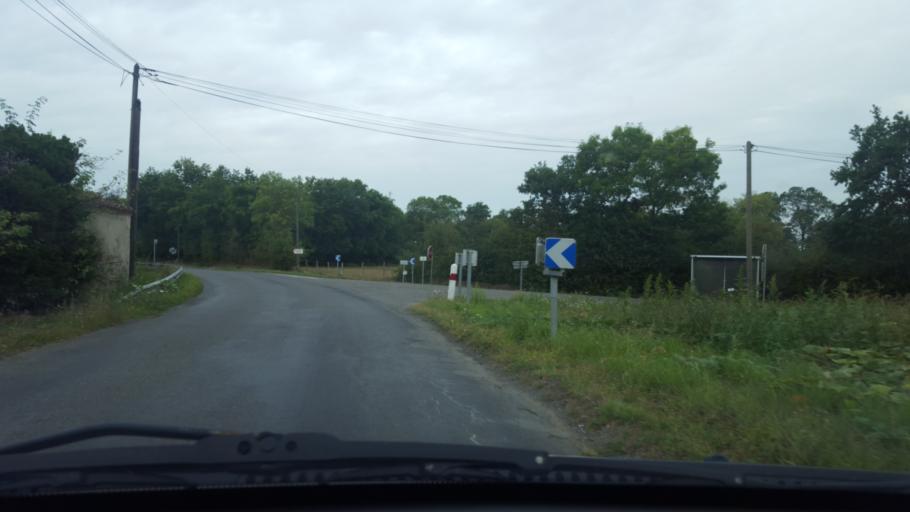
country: FR
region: Pays de la Loire
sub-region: Departement de la Loire-Atlantique
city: Saint-Philbert-de-Grand-Lieu
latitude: 46.9982
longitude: -1.6489
